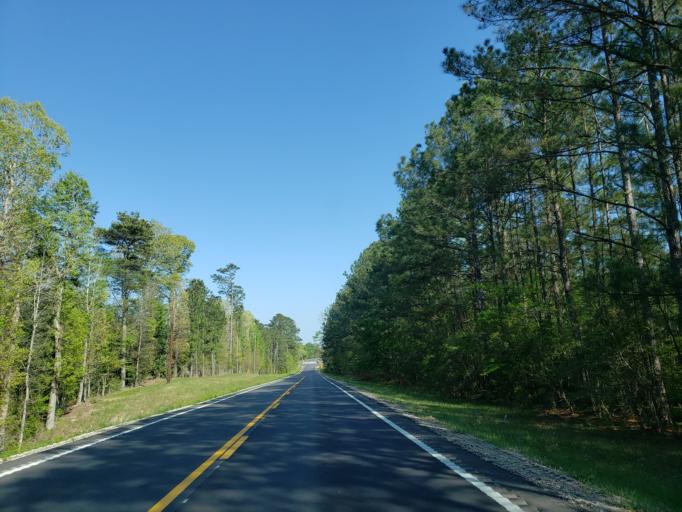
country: US
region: Mississippi
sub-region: Perry County
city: New Augusta
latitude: 31.1838
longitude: -88.9487
